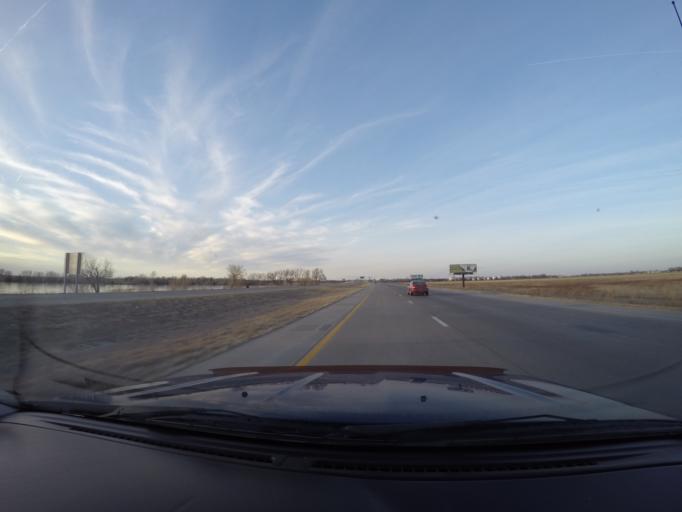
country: US
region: Kansas
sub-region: Saline County
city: Salina
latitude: 38.8315
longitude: -97.6414
